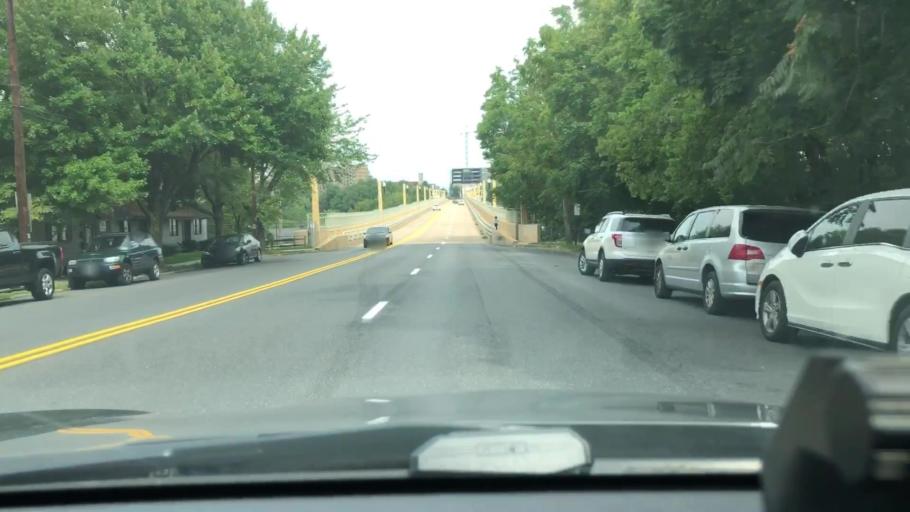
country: US
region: Pennsylvania
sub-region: Lehigh County
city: Allentown
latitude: 40.5933
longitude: -75.4698
